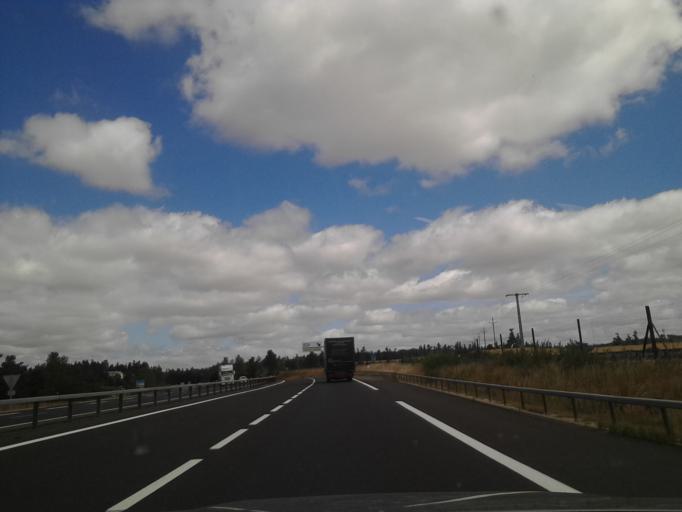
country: FR
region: Languedoc-Roussillon
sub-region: Departement de la Lozere
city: Aumont-Aubrac
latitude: 44.6965
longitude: 3.2819
